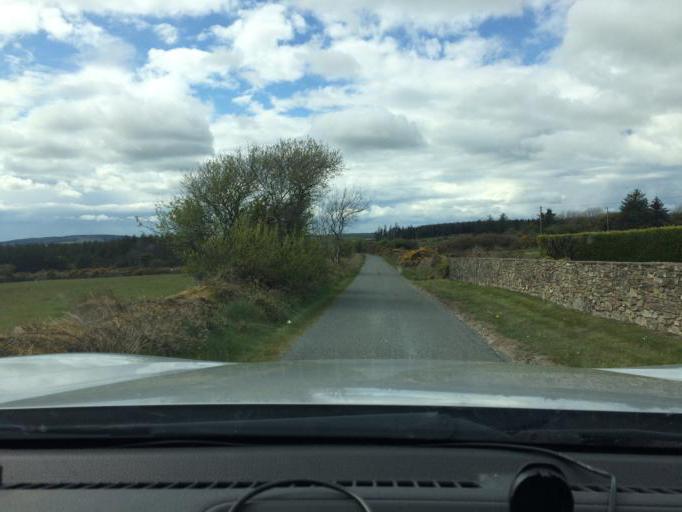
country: IE
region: Munster
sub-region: Waterford
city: Dungarvan
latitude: 52.0404
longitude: -7.6327
